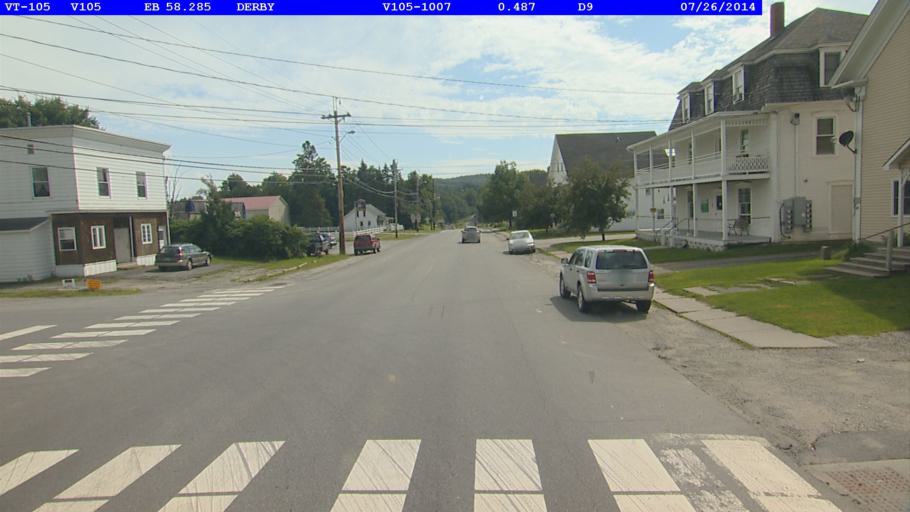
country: US
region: Vermont
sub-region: Orleans County
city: Newport
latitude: 44.9478
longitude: -72.1336
